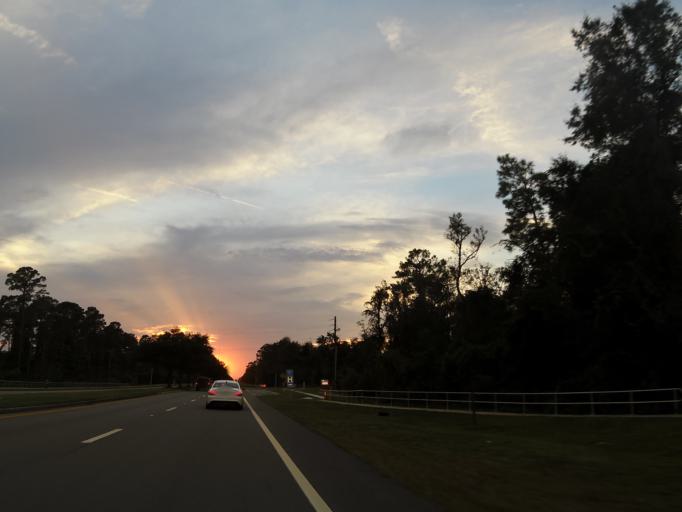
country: US
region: Florida
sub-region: Saint Johns County
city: Fruit Cove
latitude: 30.1091
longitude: -81.5639
